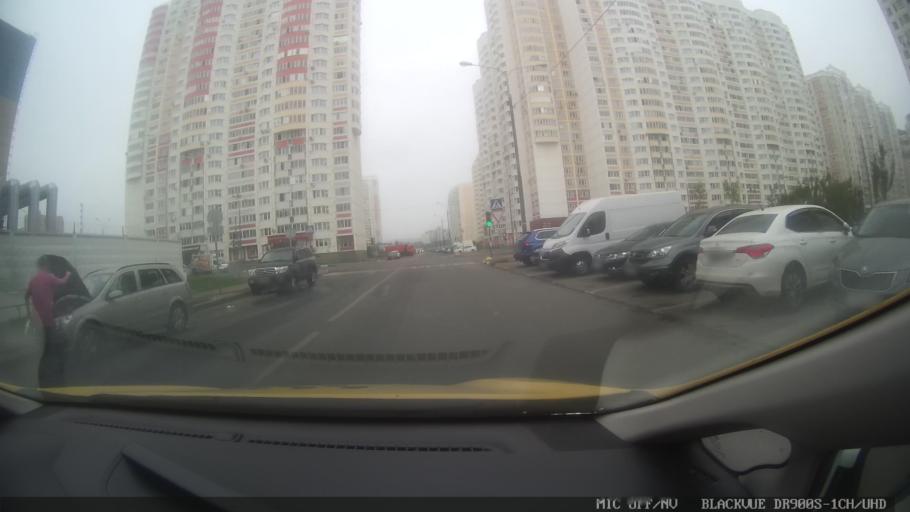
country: RU
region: Moscow
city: Nekrasovka
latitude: 55.6866
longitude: 37.9078
